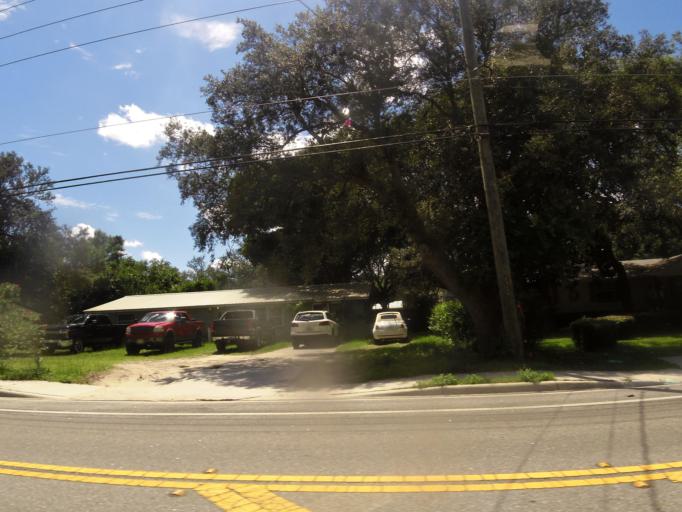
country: US
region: Florida
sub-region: Nassau County
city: Fernandina Beach
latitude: 30.6606
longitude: -81.4529
